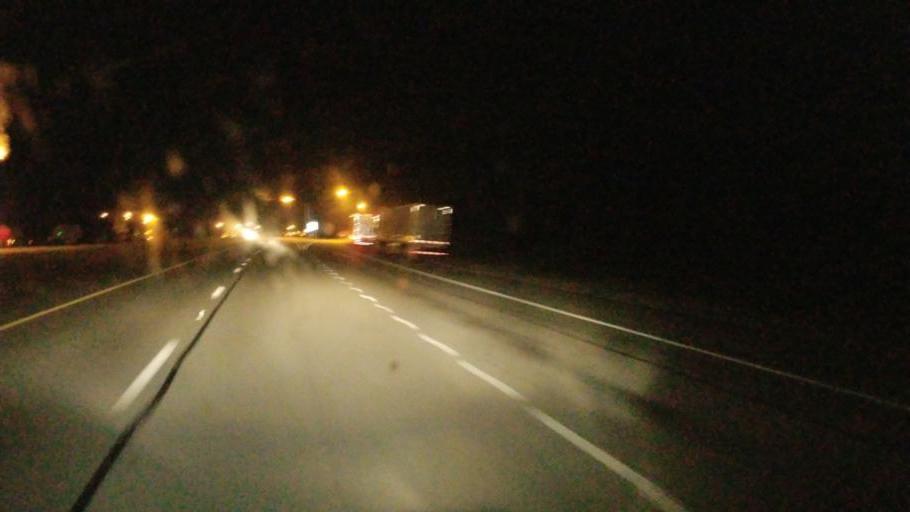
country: US
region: Ohio
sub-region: Putnam County
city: Columbus Grove
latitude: 40.8246
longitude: -84.0574
